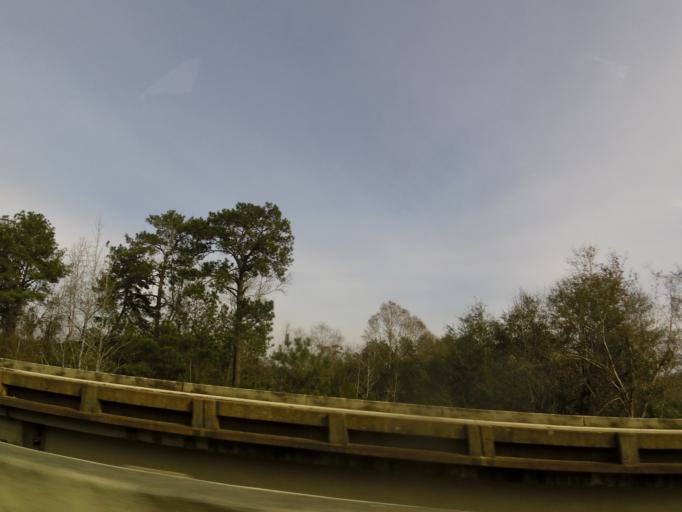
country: US
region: Alabama
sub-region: Dale County
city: Newton
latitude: 31.3577
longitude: -85.5590
